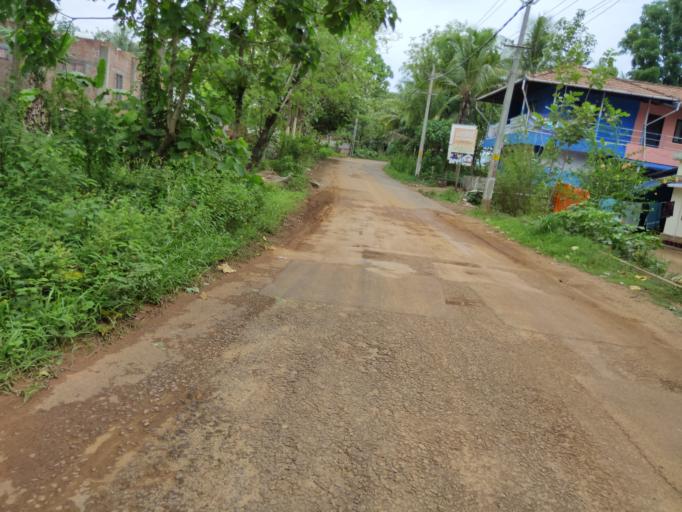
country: IN
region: Kerala
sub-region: Malappuram
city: Manjeri
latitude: 11.2473
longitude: 76.2488
